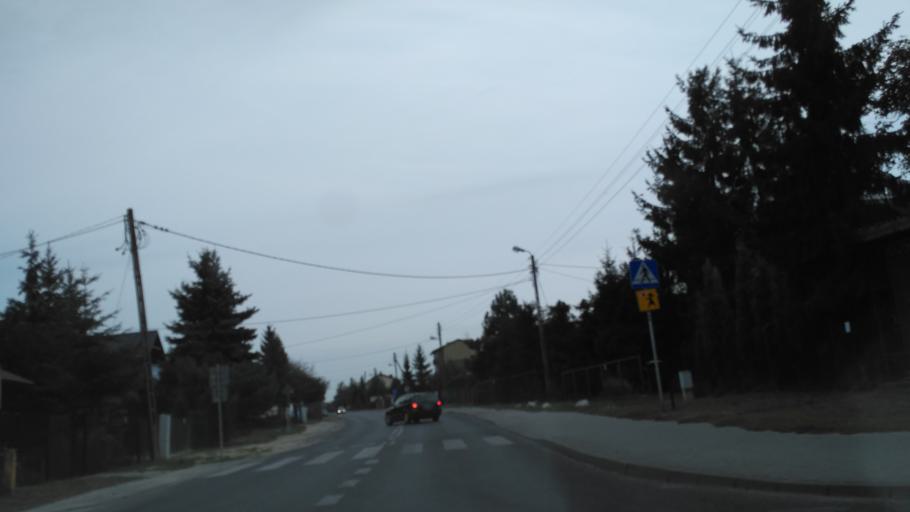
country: PL
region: Lublin Voivodeship
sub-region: Powiat lubelski
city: Lublin
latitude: 51.2203
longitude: 22.5886
